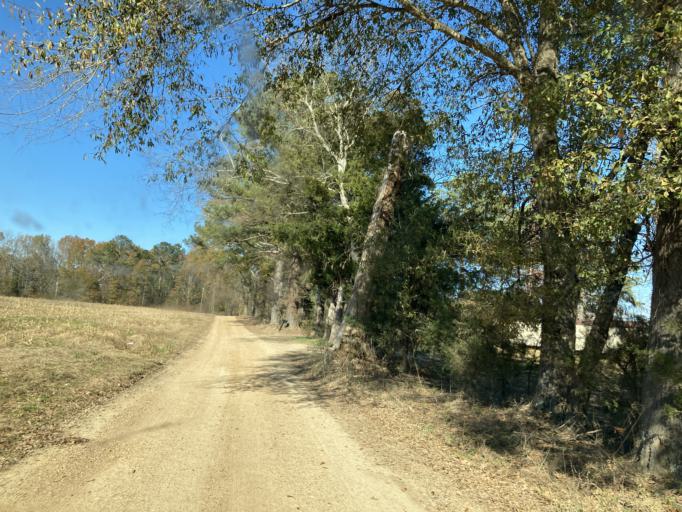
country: US
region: Mississippi
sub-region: Holmes County
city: Pickens
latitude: 32.8581
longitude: -90.0069
